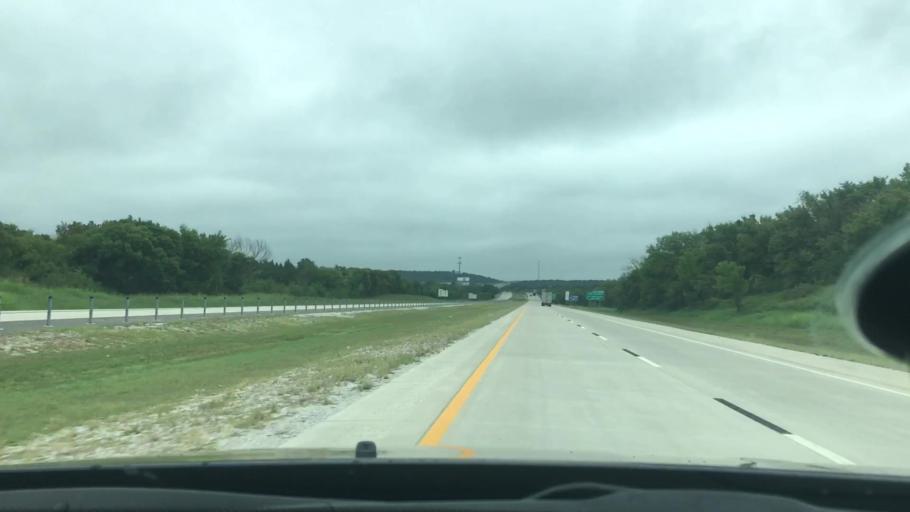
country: US
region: Oklahoma
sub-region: Okmulgee County
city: Henryetta
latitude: 35.4339
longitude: -96.0028
